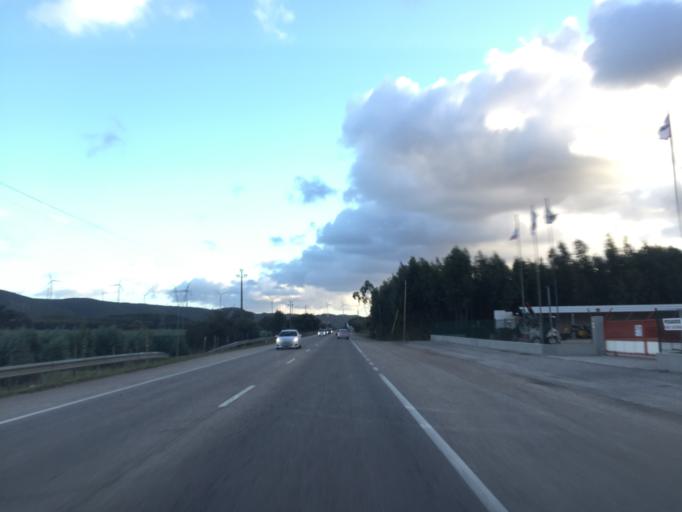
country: PT
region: Leiria
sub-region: Alcobaca
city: Benedita
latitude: 39.4150
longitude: -8.9630
